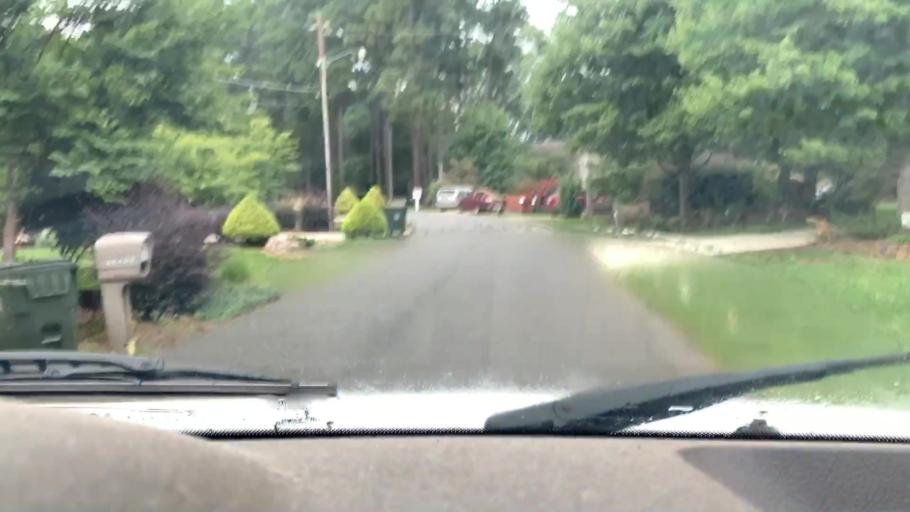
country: US
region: North Carolina
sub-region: Mecklenburg County
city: Cornelius
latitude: 35.4908
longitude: -80.9108
